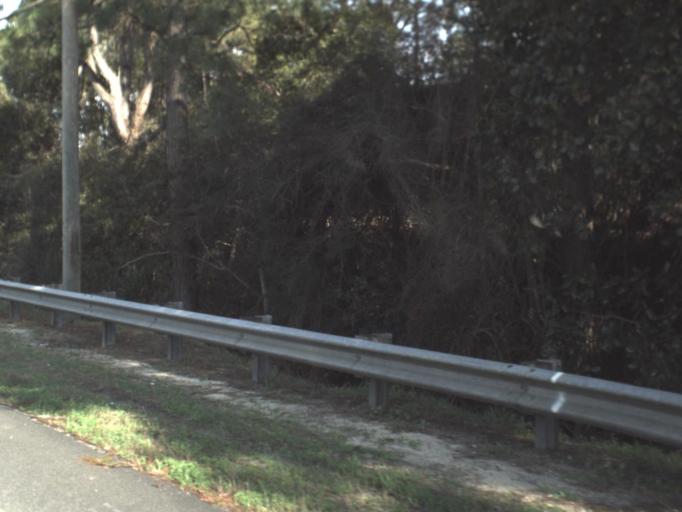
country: US
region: Florida
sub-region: Bay County
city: Hiland Park
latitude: 30.2462
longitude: -85.5606
